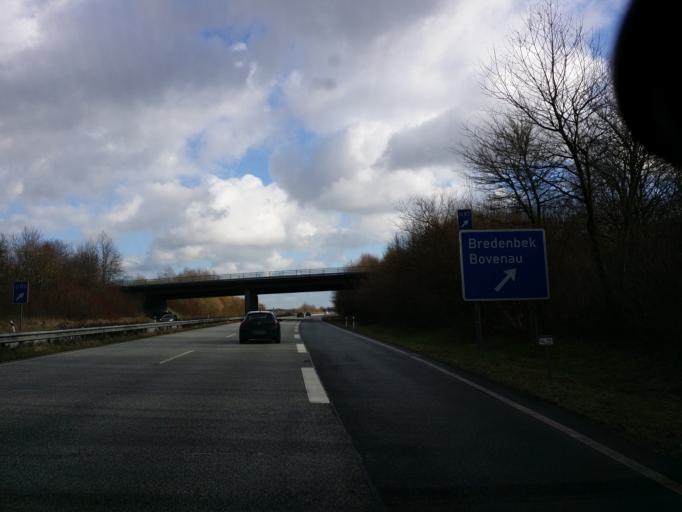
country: DE
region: Schleswig-Holstein
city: Bredenbek
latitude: 54.3177
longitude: 9.8523
